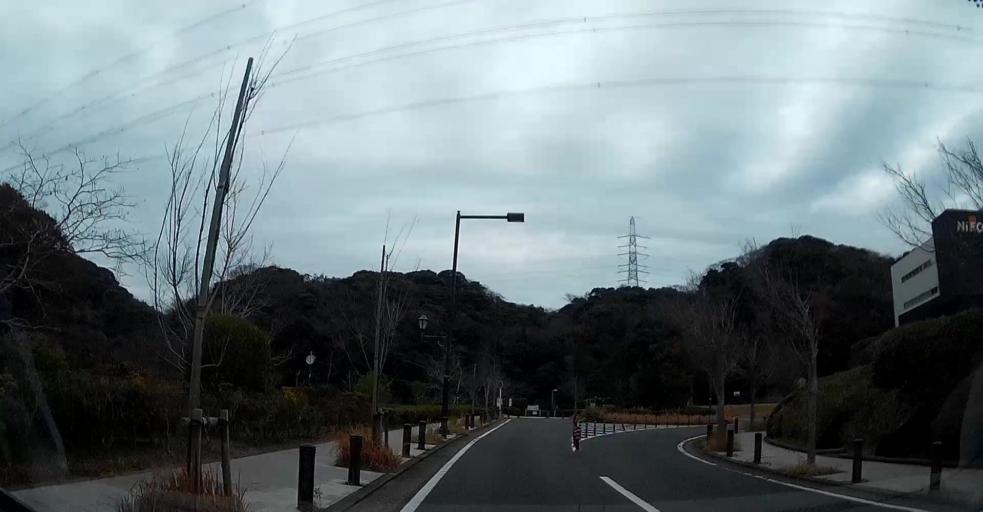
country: JP
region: Kanagawa
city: Yokosuka
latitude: 35.2255
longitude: 139.6752
